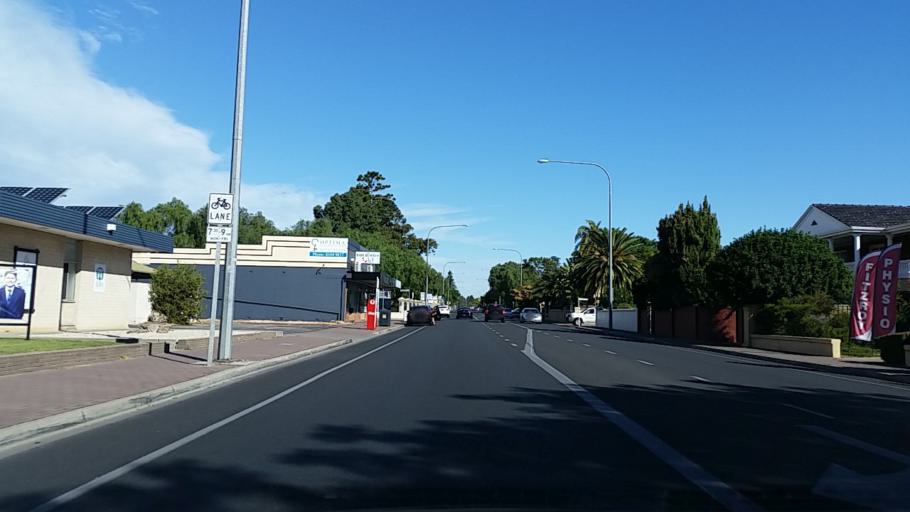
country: AU
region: South Australia
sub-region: Prospect
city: Prospect
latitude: -34.8934
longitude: 138.5945
